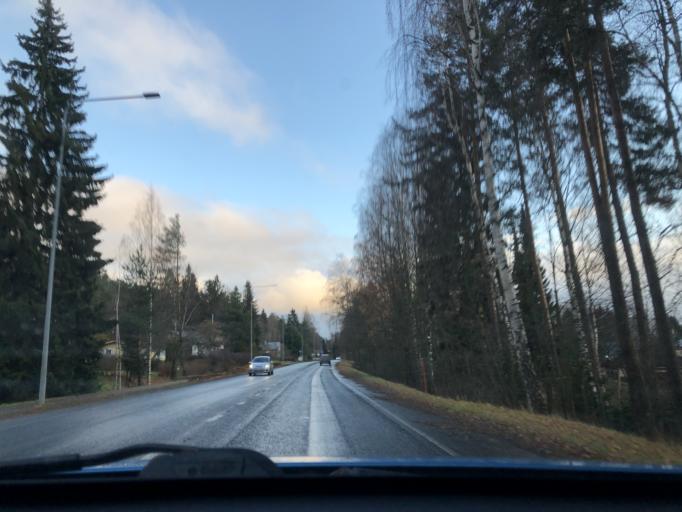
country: FI
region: Pirkanmaa
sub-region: Tampere
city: Kangasala
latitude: 61.4683
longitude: 24.0461
